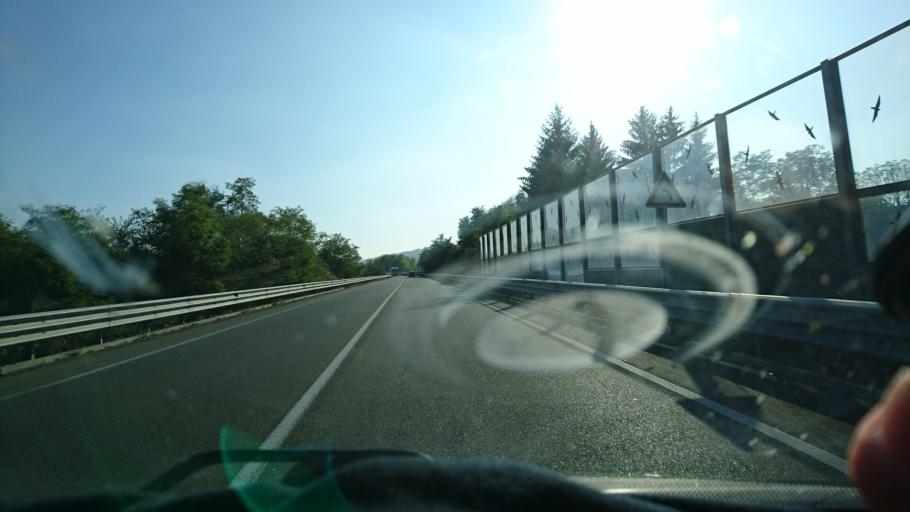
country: IT
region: Piedmont
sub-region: Provincia di Alessandria
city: Strevi
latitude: 44.6924
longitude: 8.5267
